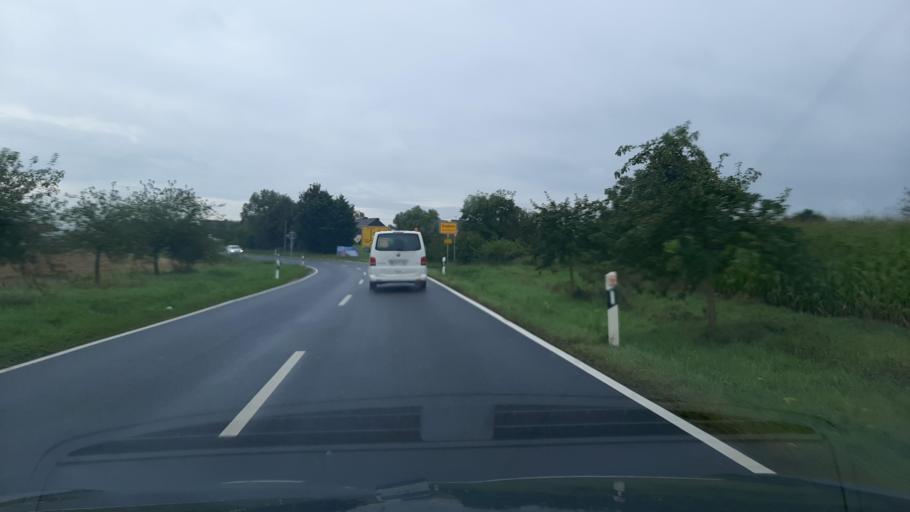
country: DE
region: Rheinland-Pfalz
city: Badem
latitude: 50.0089
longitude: 6.6092
